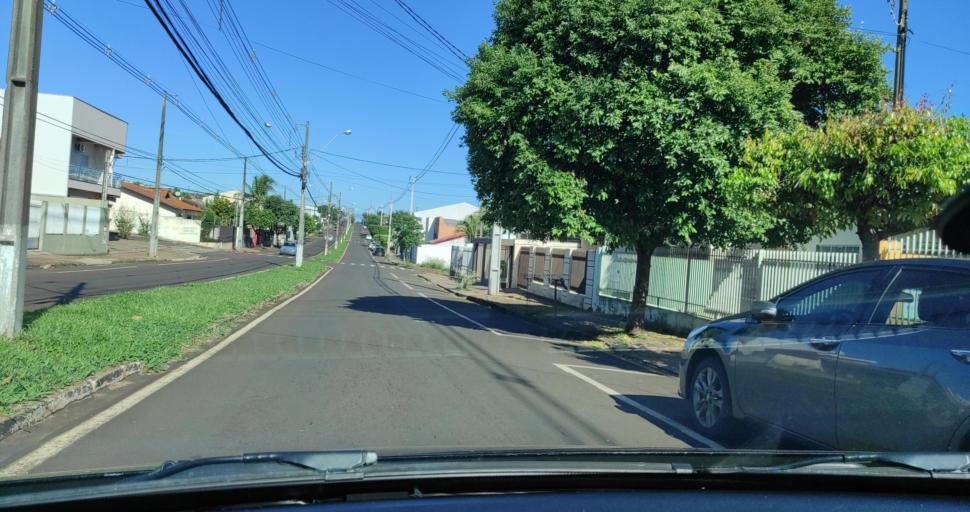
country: BR
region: Parana
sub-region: Ibipora
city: Ibipora
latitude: -23.2736
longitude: -51.0653
